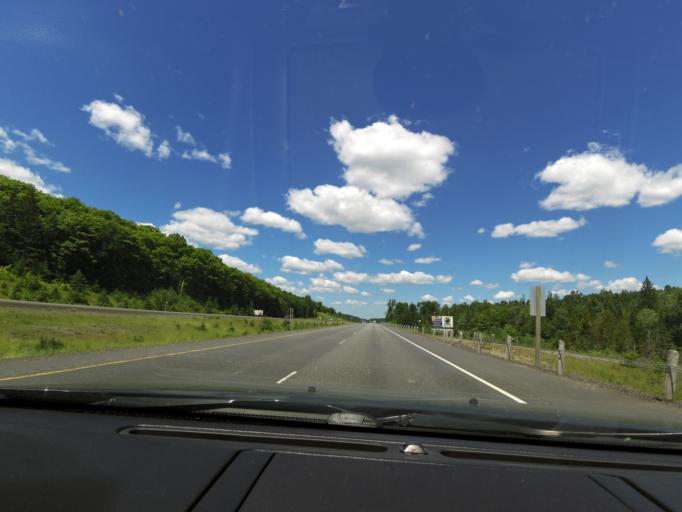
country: CA
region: Ontario
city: Huntsville
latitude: 45.4666
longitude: -79.2630
